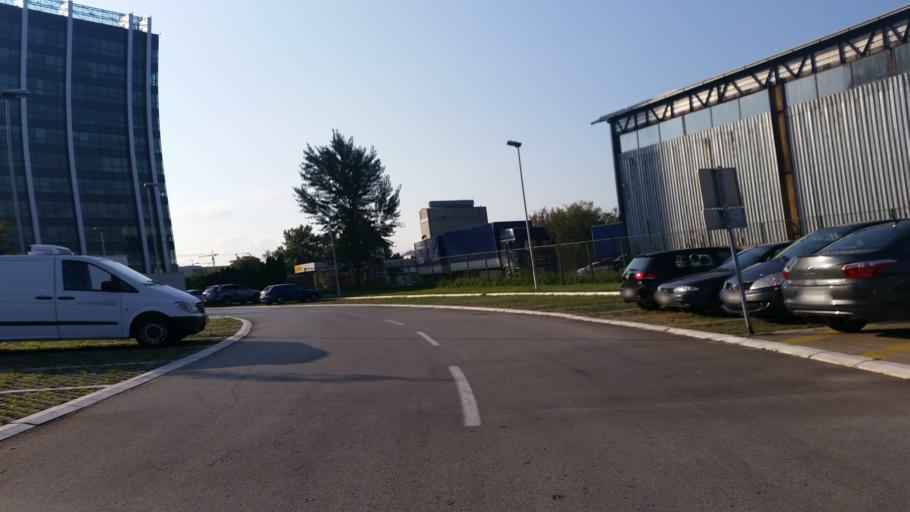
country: RS
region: Central Serbia
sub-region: Belgrade
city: Novi Beograd
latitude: 44.8128
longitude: 20.3947
